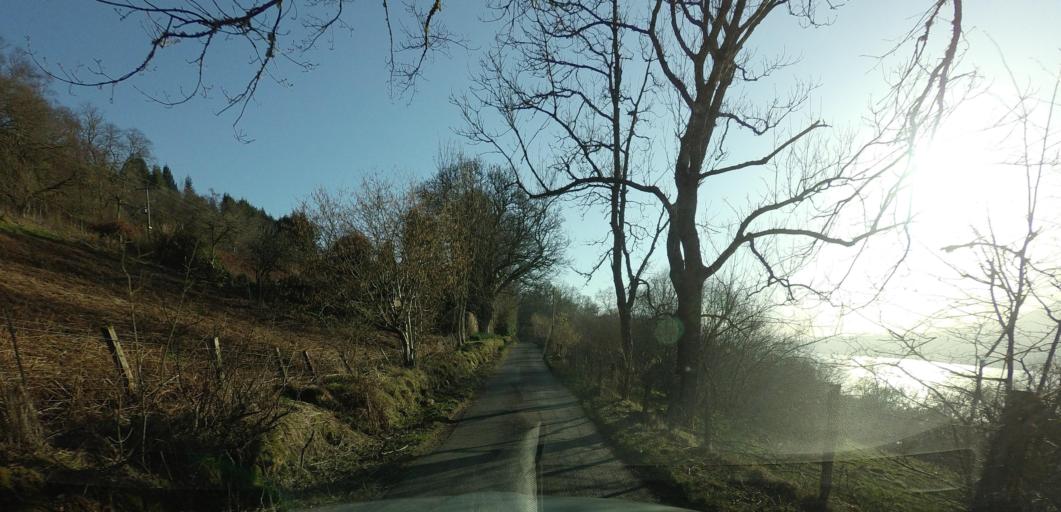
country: GB
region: Scotland
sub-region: Perth and Kinross
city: Comrie
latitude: 56.5465
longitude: -4.0980
